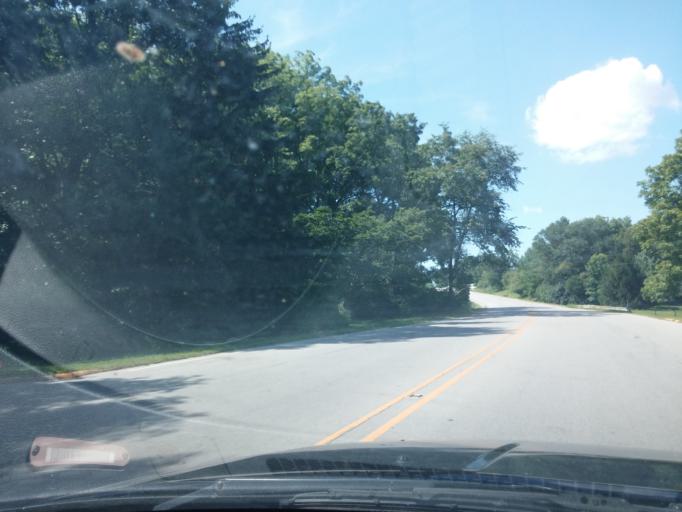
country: US
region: Indiana
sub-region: Tippecanoe County
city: West Lafayette
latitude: 40.4278
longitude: -86.9306
